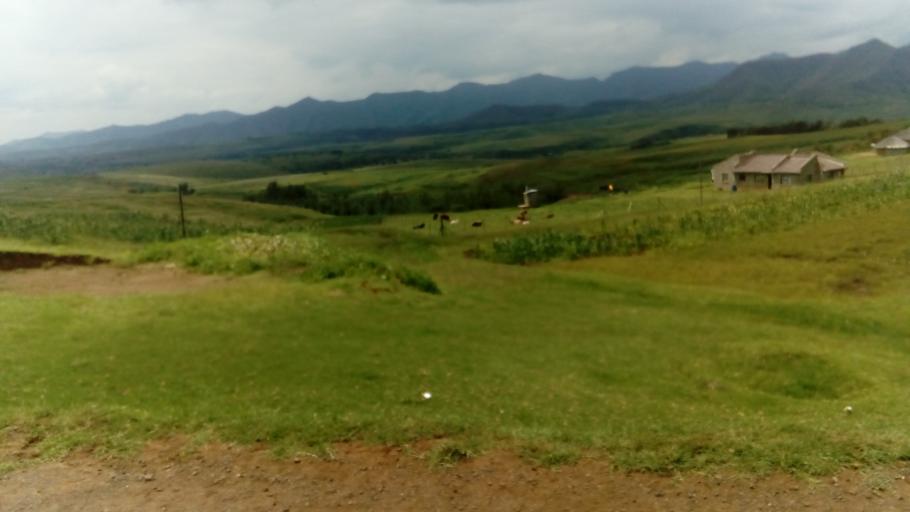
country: LS
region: Leribe
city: Leribe
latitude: -29.0249
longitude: 28.2276
